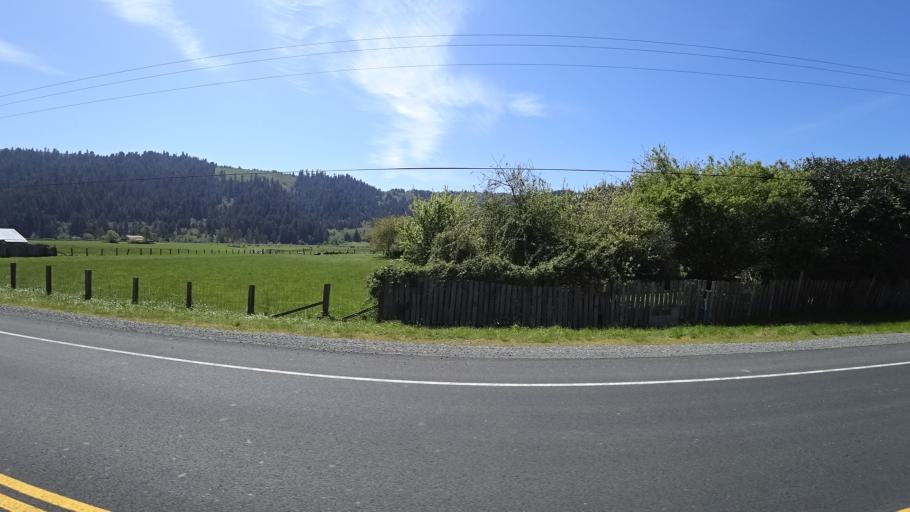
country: US
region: California
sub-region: Humboldt County
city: Westhaven-Moonstone
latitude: 41.2846
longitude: -124.0718
